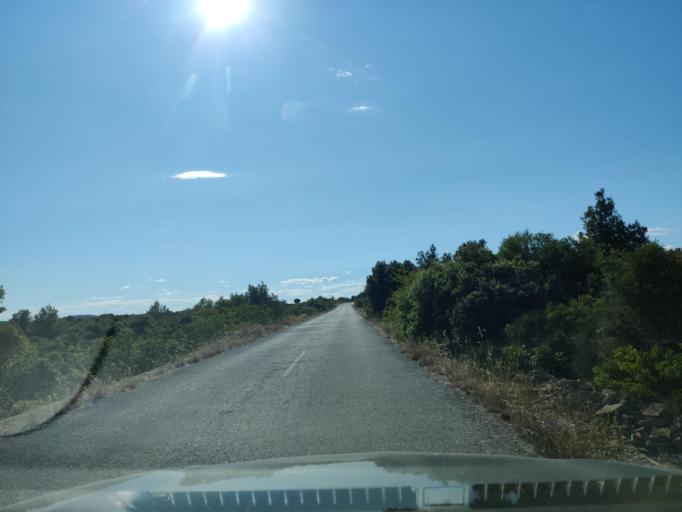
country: HR
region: Sibensko-Kniniska
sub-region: Grad Sibenik
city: Sibenik
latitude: 43.7398
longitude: 15.8619
